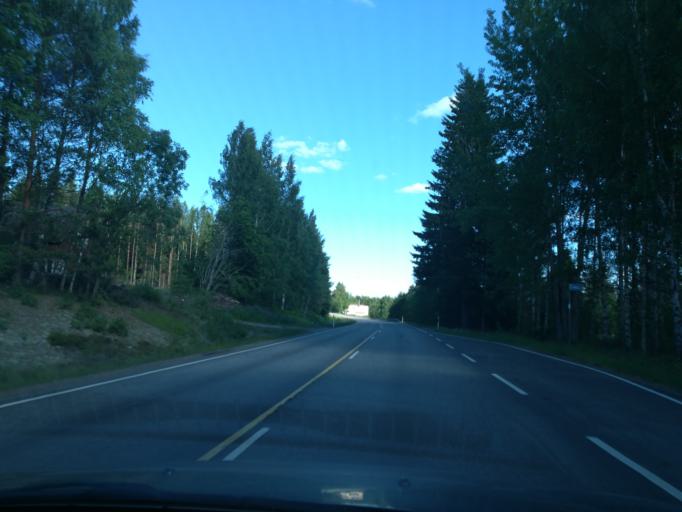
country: FI
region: South Karelia
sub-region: Imatra
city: Ruokolahti
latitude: 61.3742
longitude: 28.6606
